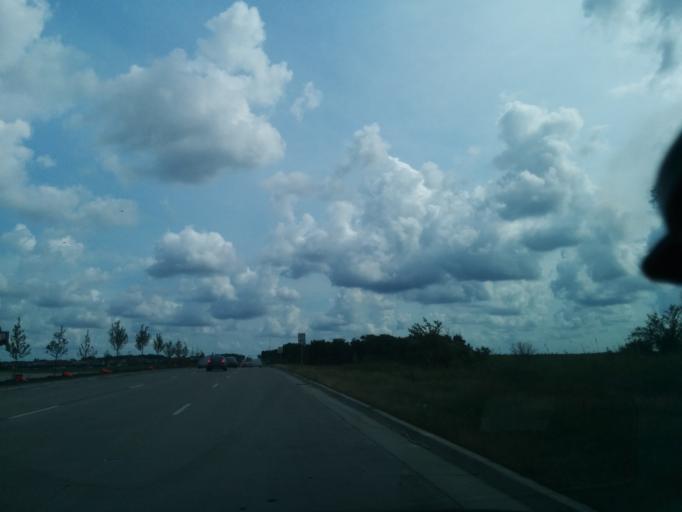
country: US
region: Illinois
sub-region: Cook County
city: Orland Hills
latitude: 41.5864
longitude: -87.8524
